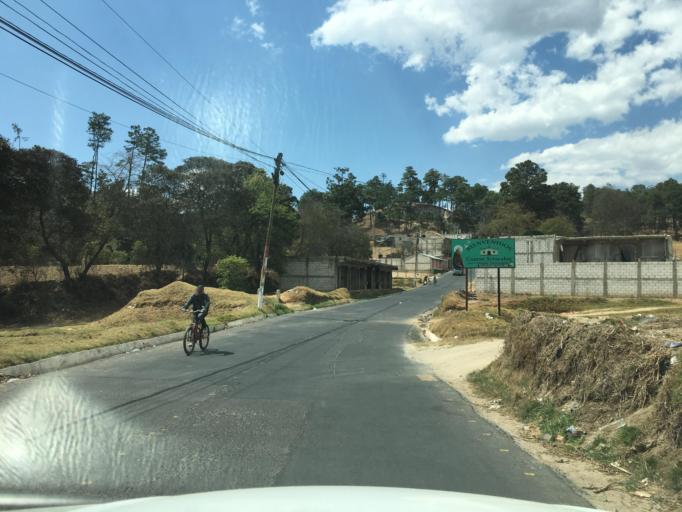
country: GT
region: Quetzaltenango
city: Salcaja
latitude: 14.9055
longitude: -91.4594
